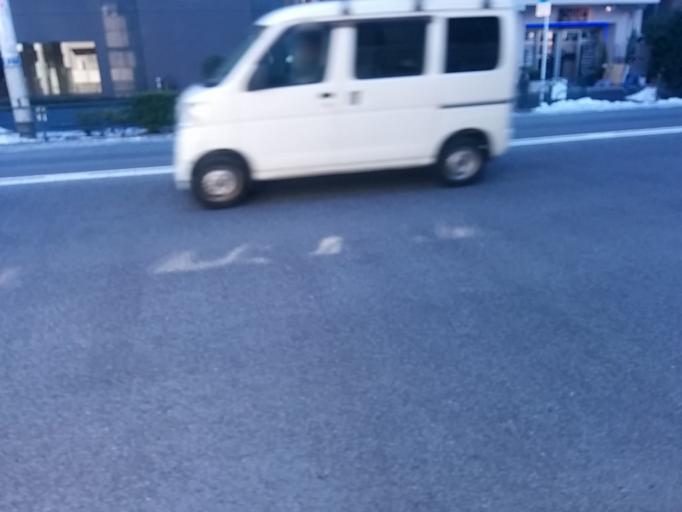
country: JP
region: Tokyo
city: Tokyo
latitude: 35.7332
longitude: 139.7563
